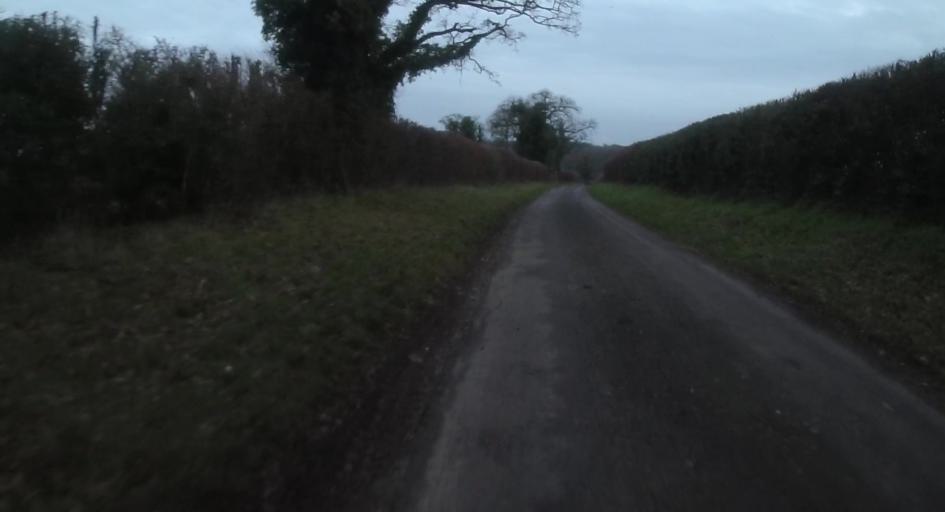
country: GB
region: England
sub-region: Hampshire
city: Overton
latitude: 51.2532
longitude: -1.3059
